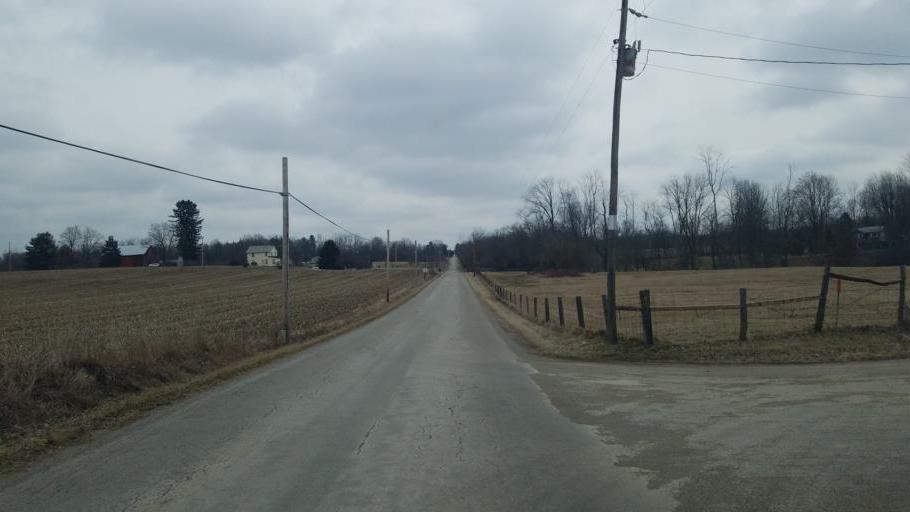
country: US
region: Ohio
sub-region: Crawford County
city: Galion
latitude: 40.6396
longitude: -82.7974
